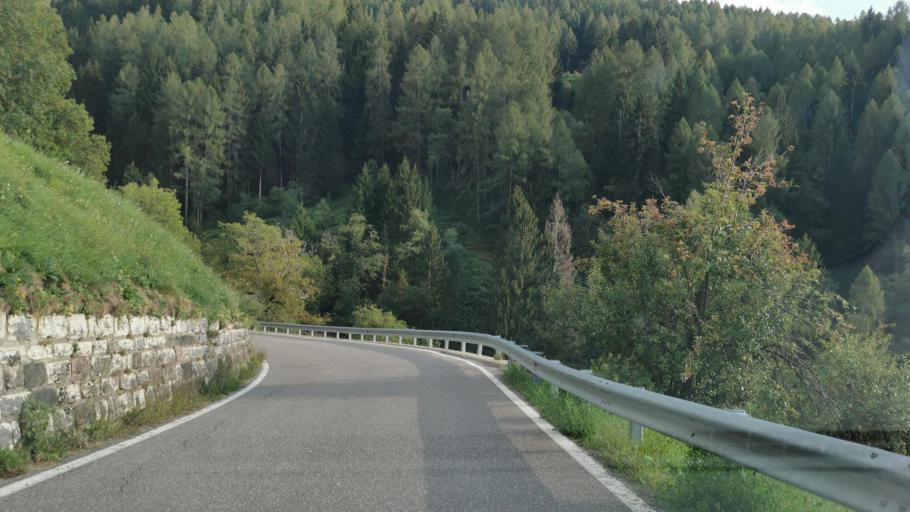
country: IT
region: Trentino-Alto Adige
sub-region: Provincia di Trento
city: Sant'Orsola Terme
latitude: 46.0965
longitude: 11.3117
